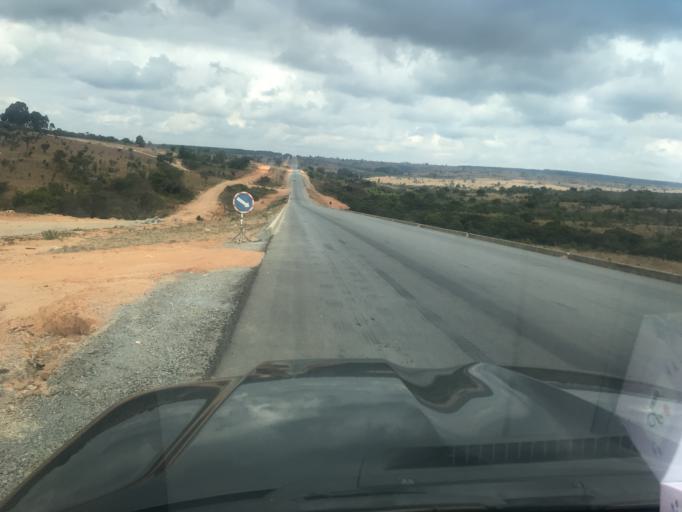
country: TZ
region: Iringa
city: Makungu
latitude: -8.3412
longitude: 35.2496
